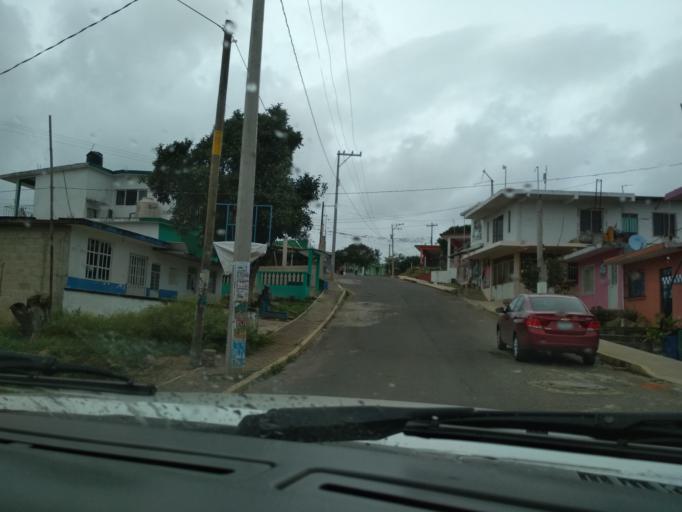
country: MX
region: Veracruz
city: El Castillo
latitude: 19.5385
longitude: -96.8209
